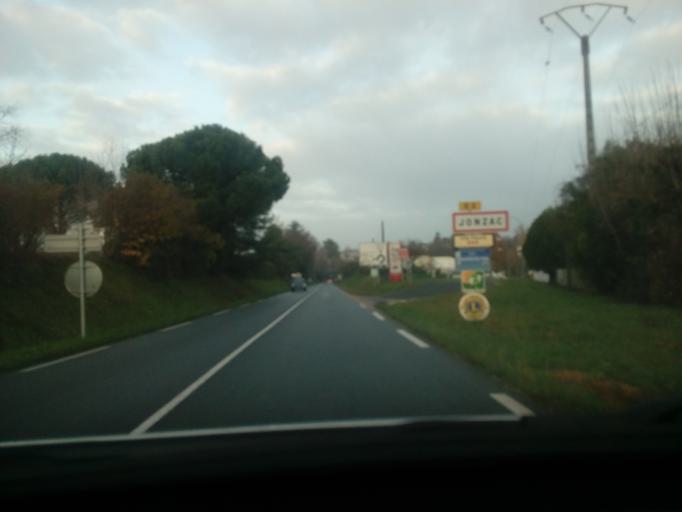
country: FR
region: Poitou-Charentes
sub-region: Departement de la Charente-Maritime
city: Jonzac
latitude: 45.4443
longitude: -0.4225
